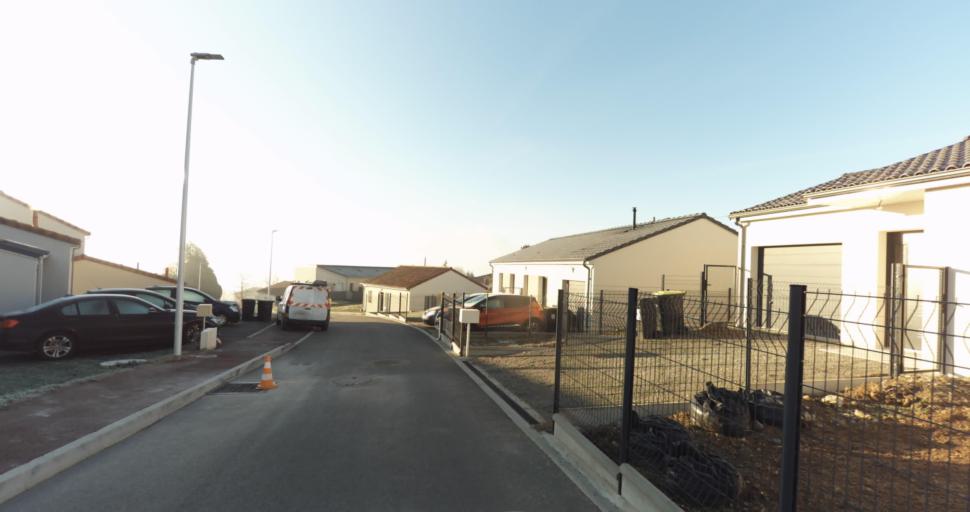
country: FR
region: Limousin
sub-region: Departement de la Haute-Vienne
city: Aixe-sur-Vienne
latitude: 45.8009
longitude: 1.1465
